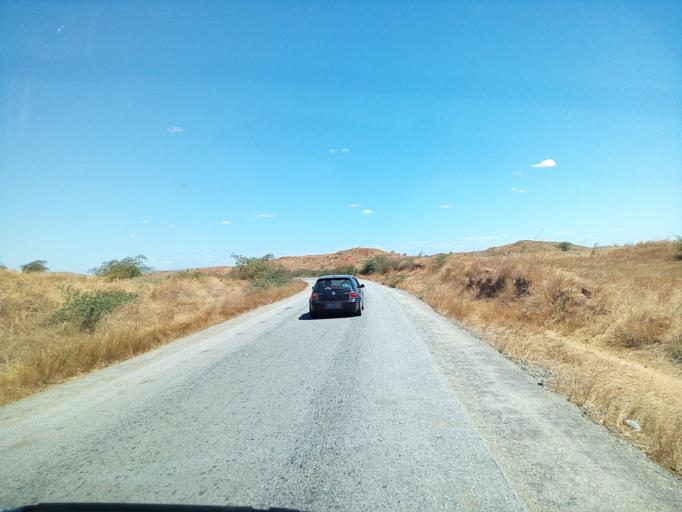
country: MG
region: Betsiboka
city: Maevatanana
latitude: -17.1093
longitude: 46.8103
